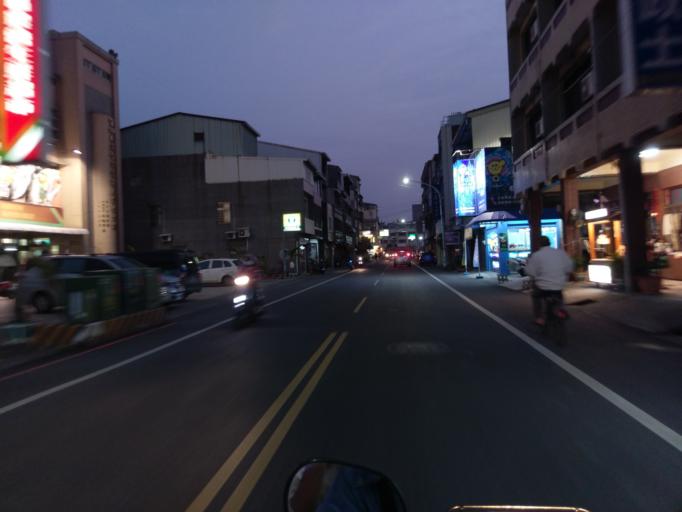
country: TW
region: Taiwan
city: Xinying
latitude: 23.1938
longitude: 120.3183
